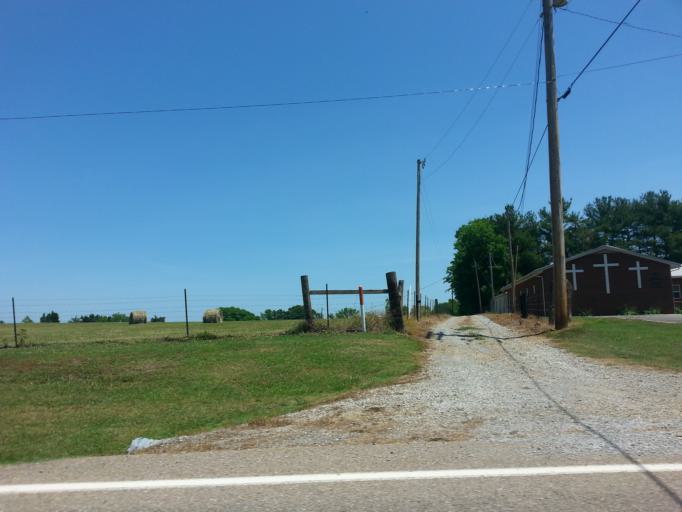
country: US
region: Tennessee
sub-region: Jefferson County
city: Dandridge
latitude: 35.9917
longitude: -83.3915
